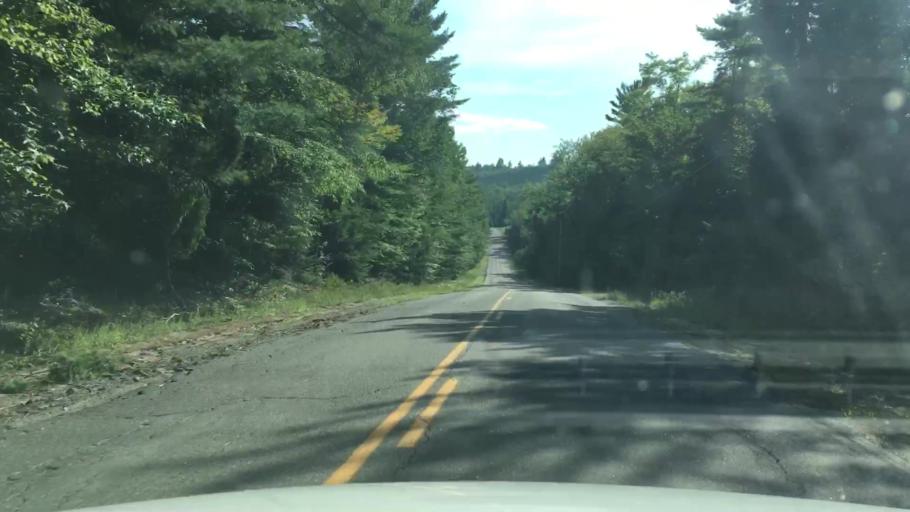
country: US
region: Maine
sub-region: Penobscot County
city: Enfield
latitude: 45.2974
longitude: -68.5533
